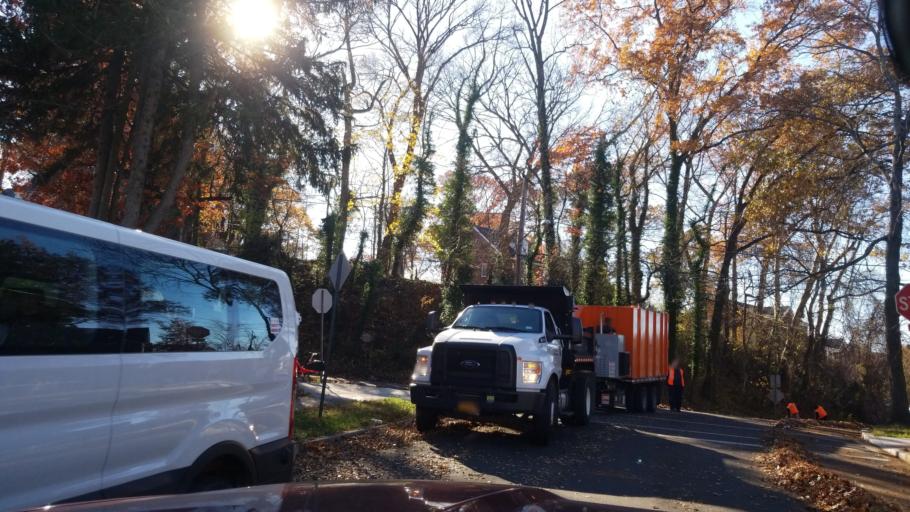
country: US
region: Maryland
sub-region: Prince George's County
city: Mount Rainier
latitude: 38.9330
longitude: -76.9624
